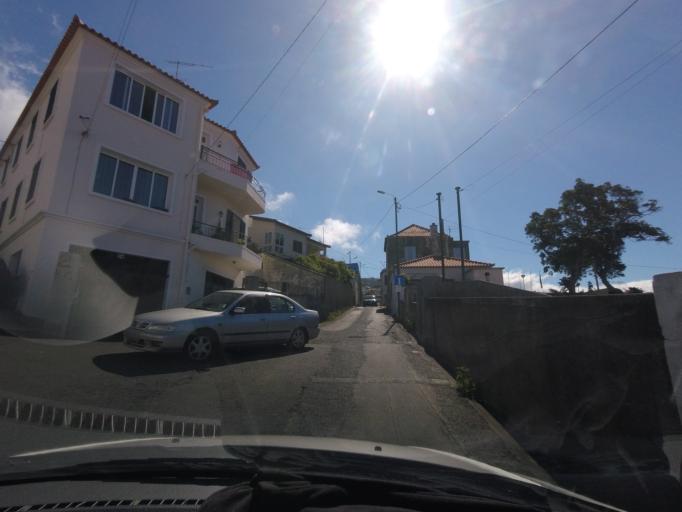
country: PT
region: Madeira
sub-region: Funchal
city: Funchal
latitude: 32.6473
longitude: -16.8906
